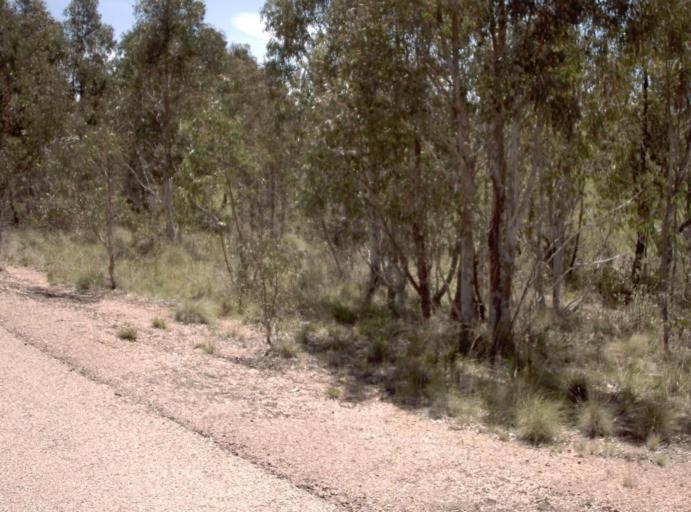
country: AU
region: New South Wales
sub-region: Snowy River
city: Jindabyne
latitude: -37.0558
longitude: 148.2593
